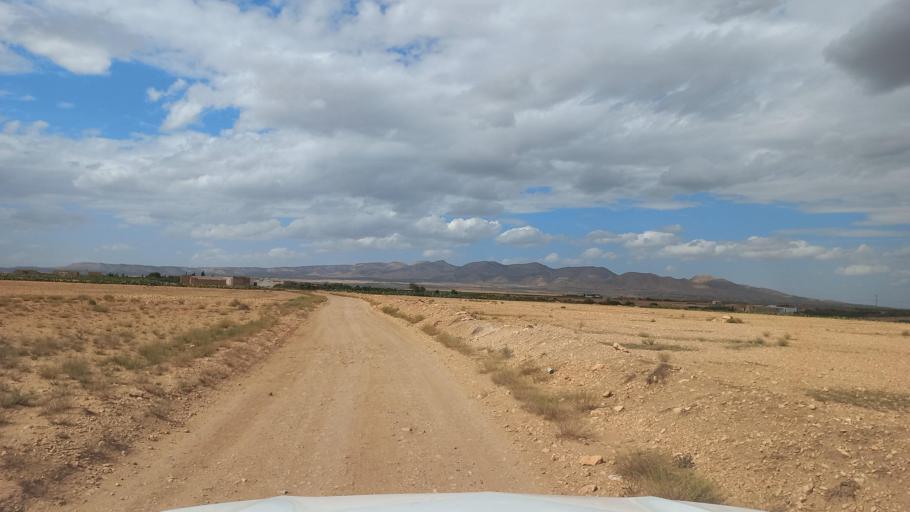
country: TN
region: Al Qasrayn
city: Sbiba
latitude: 35.3820
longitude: 9.0986
